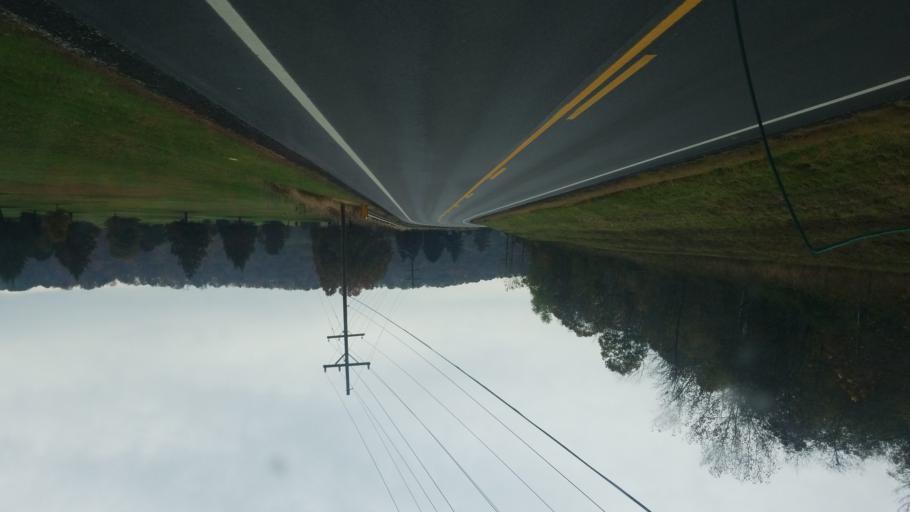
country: US
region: Ohio
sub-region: Washington County
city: Beverly
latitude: 39.5490
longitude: -81.5976
